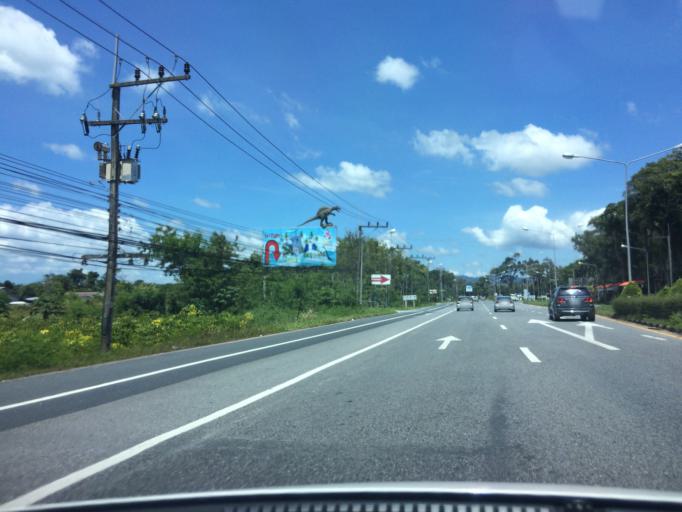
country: TH
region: Phangnga
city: Thai Mueang
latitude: 8.2233
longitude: 98.2989
